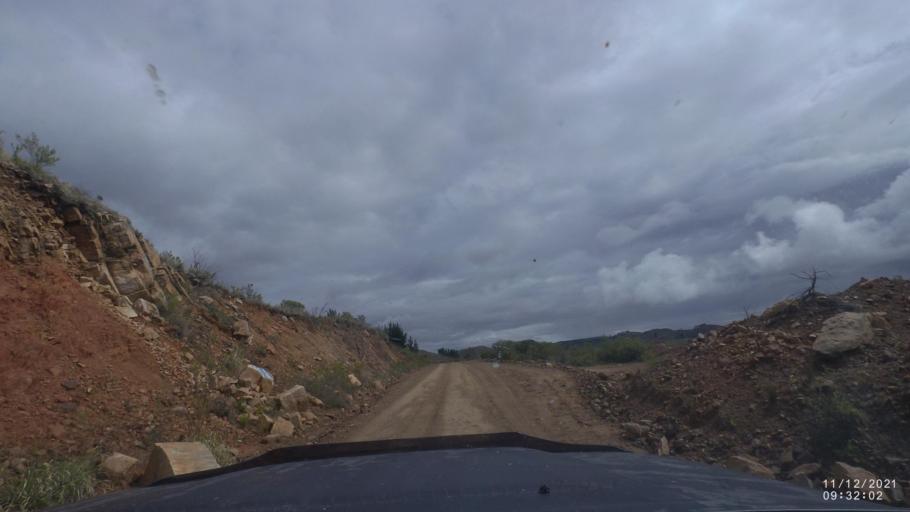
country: BO
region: Cochabamba
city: Tarata
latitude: -17.8478
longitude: -65.9894
